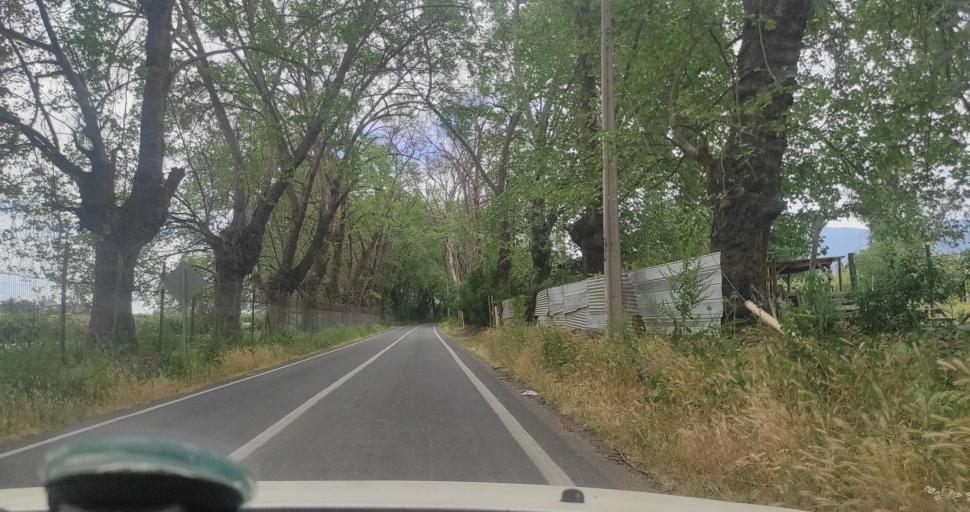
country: CL
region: Valparaiso
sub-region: Provincia de Marga Marga
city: Limache
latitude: -33.0251
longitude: -71.2403
